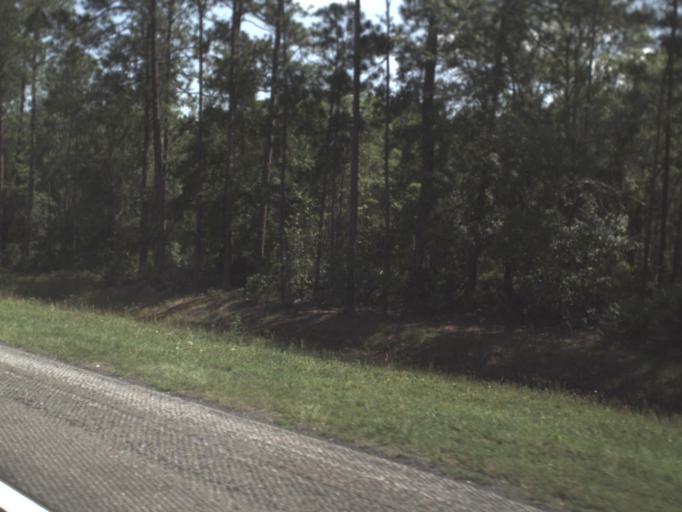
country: US
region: Florida
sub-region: Nassau County
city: Yulee
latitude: 30.5415
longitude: -81.6375
